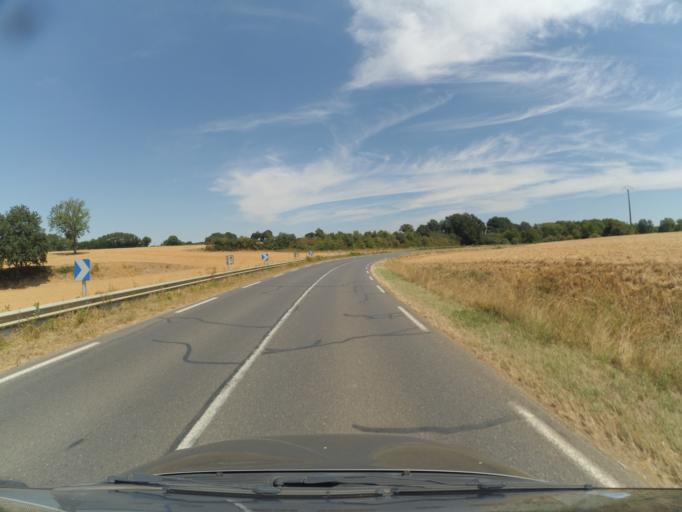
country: FR
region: Poitou-Charentes
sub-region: Departement de la Vienne
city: Lusignan
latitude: 46.4318
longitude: 0.1039
